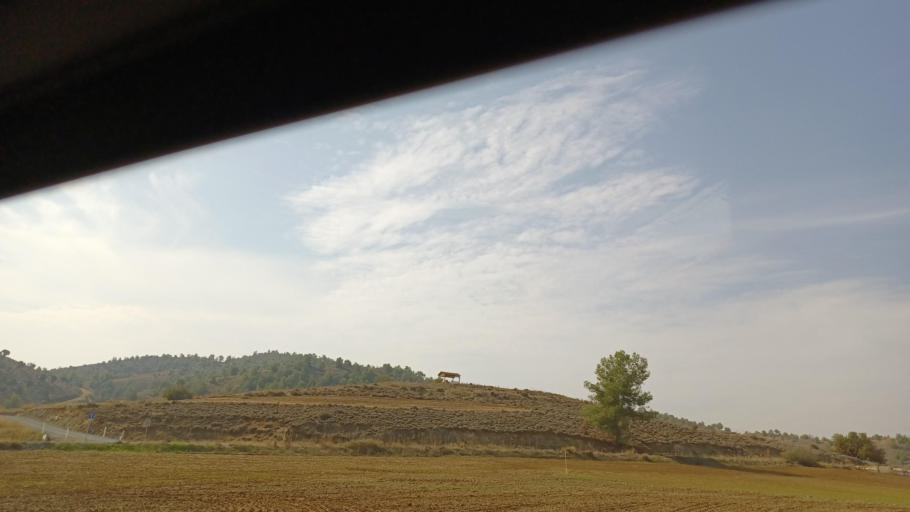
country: CY
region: Larnaka
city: Mosfiloti
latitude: 34.9664
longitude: 33.4400
